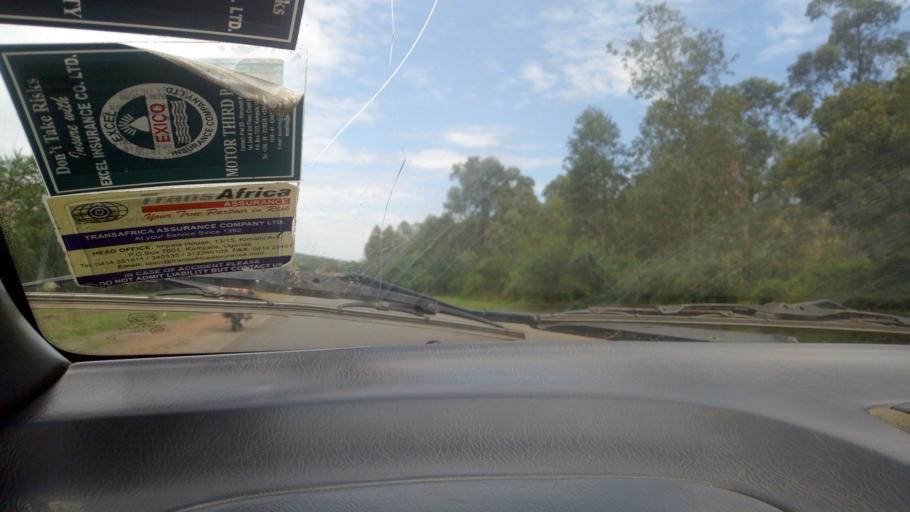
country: UG
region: Western Region
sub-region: Mbarara District
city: Bwizibwera
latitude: -0.3675
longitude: 30.5652
